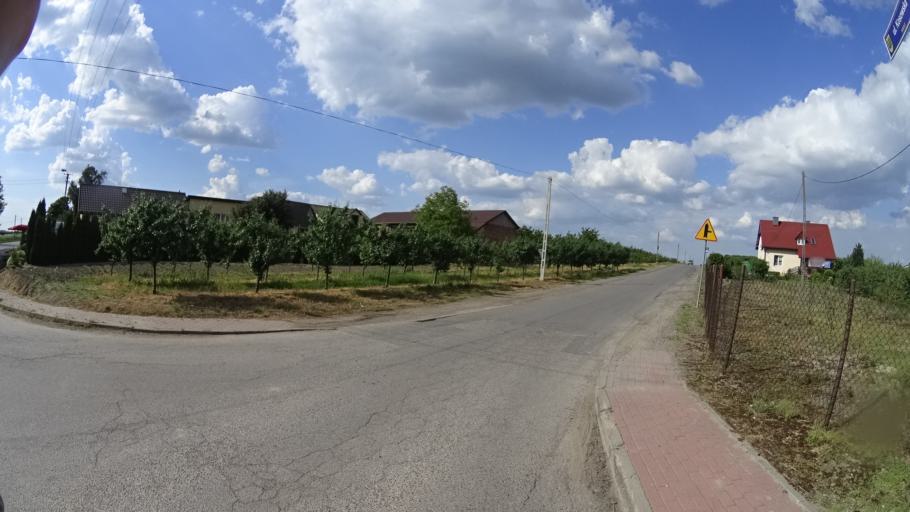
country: PL
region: Masovian Voivodeship
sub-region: Powiat piaseczynski
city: Tarczyn
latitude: 52.0366
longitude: 20.8213
